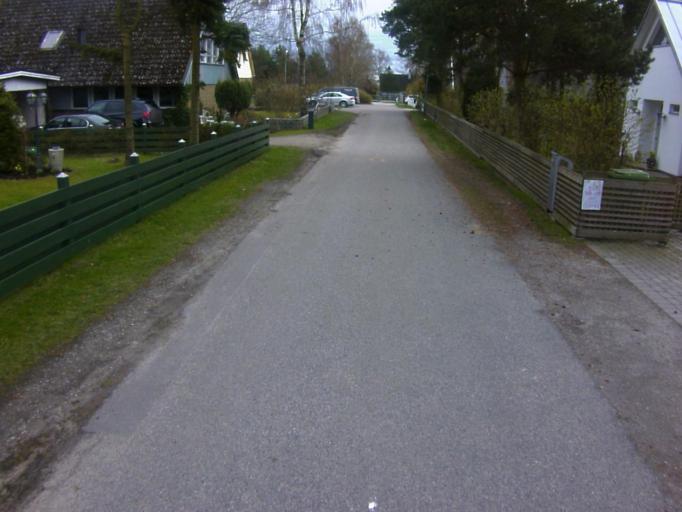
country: SE
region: Skane
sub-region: Kavlinge Kommun
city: Hofterup
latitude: 55.7955
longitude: 12.9807
